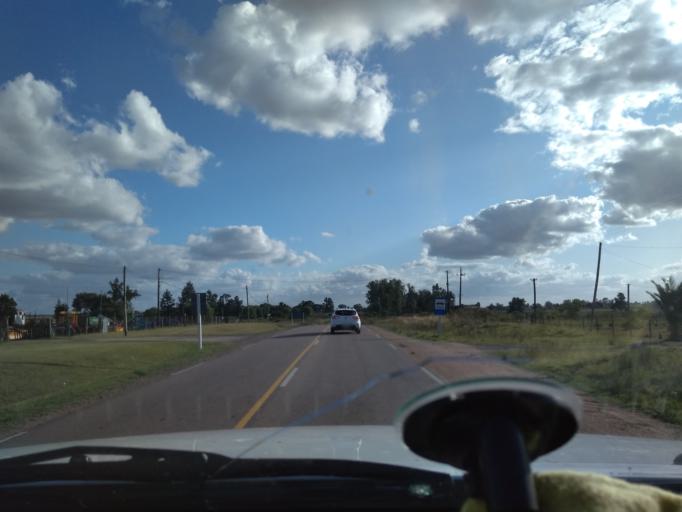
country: UY
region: Canelones
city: Tala
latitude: -34.3685
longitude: -55.7825
